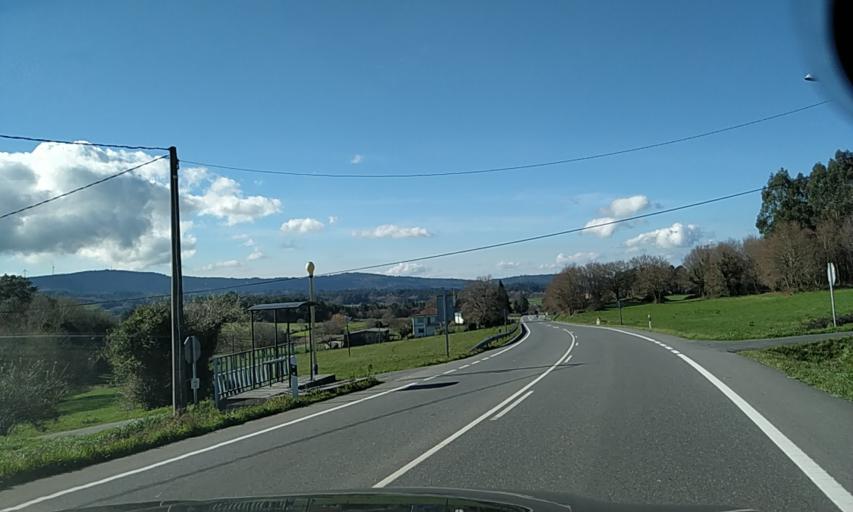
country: ES
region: Galicia
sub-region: Provincia de Pontevedra
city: Silleda
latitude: 42.7073
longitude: -8.2659
